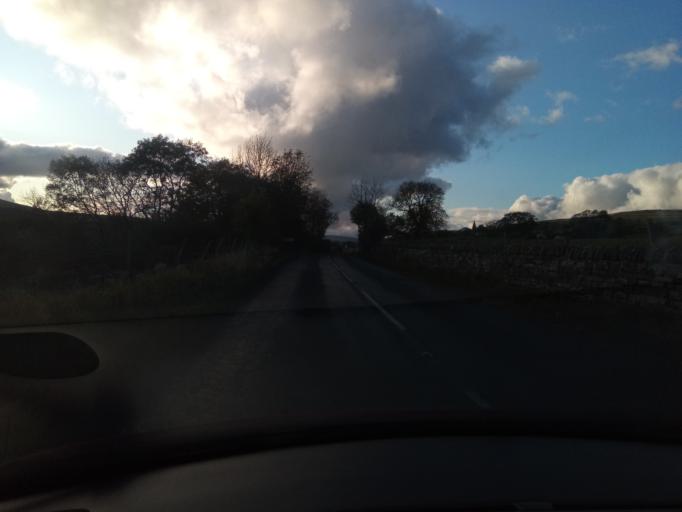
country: GB
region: England
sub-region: County Durham
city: Newbiggin
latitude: 54.7380
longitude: -2.1383
